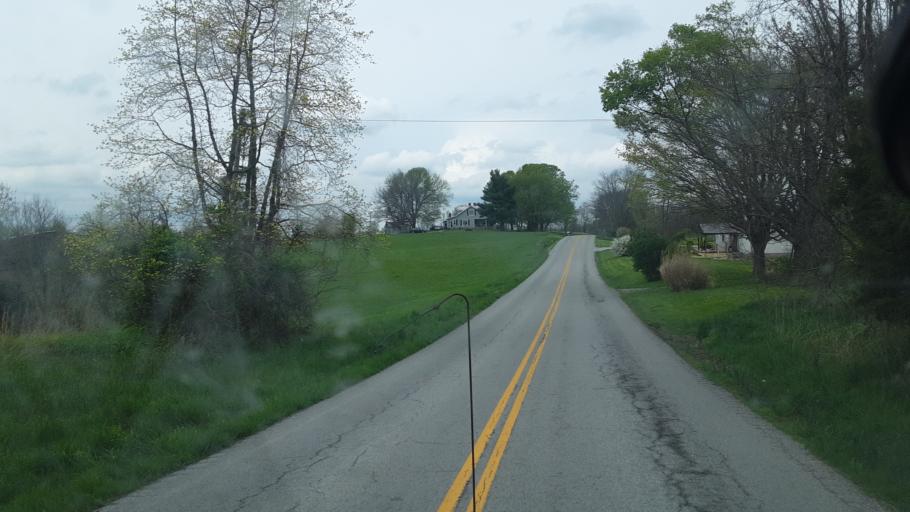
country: US
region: Kentucky
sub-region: Owen County
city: Owenton
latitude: 38.6173
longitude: -84.7865
